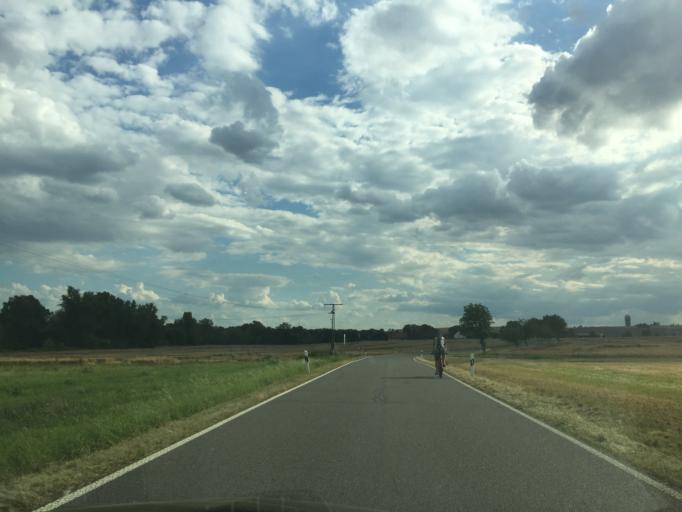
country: DE
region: Thuringia
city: Saara
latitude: 50.9471
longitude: 12.4221
